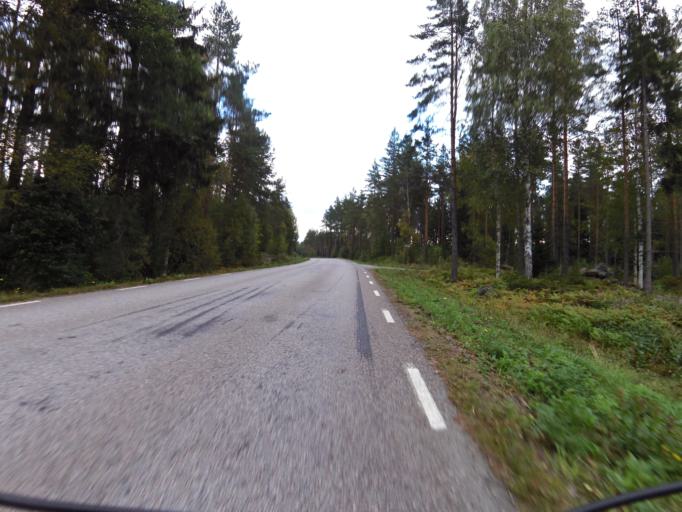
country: SE
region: Gaevleborg
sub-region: Sandvikens Kommun
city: Sandviken
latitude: 60.6594
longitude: 16.8532
